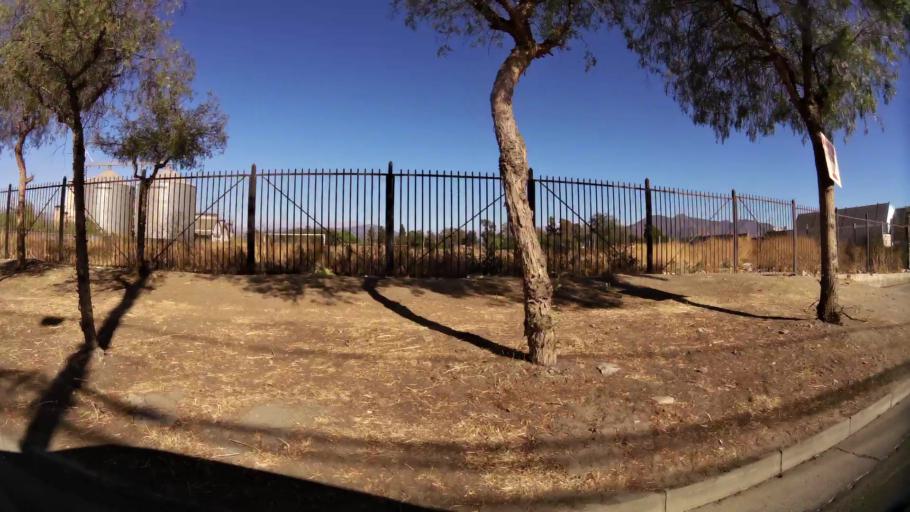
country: CL
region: O'Higgins
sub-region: Provincia de Cachapoal
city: Rancagua
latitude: -34.1804
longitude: -70.7562
